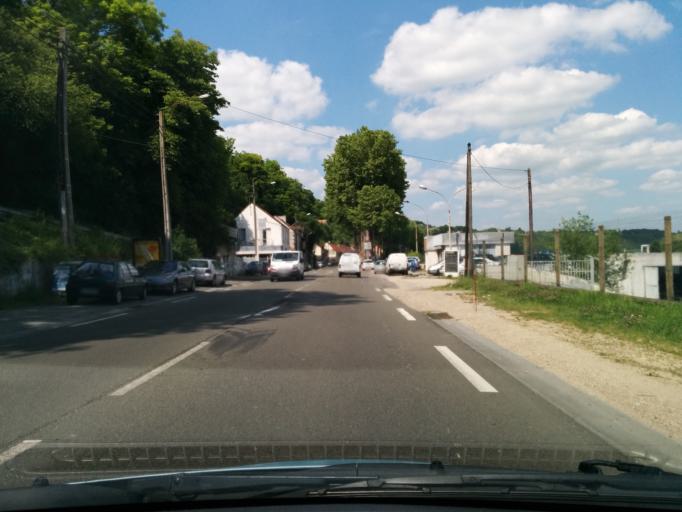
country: FR
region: Ile-de-France
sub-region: Departement des Yvelines
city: Rosny-sur-Seine
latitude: 49.0148
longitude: 1.6112
